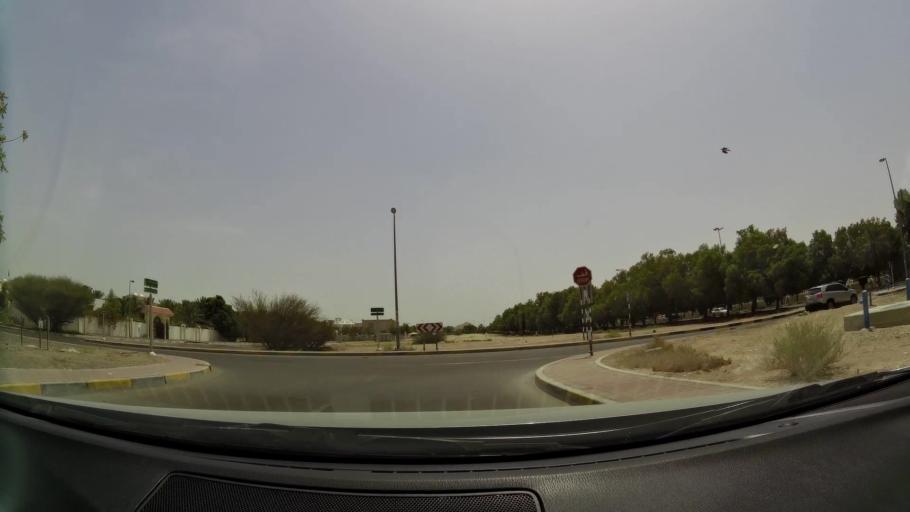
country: AE
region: Abu Dhabi
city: Al Ain
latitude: 24.1784
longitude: 55.7276
